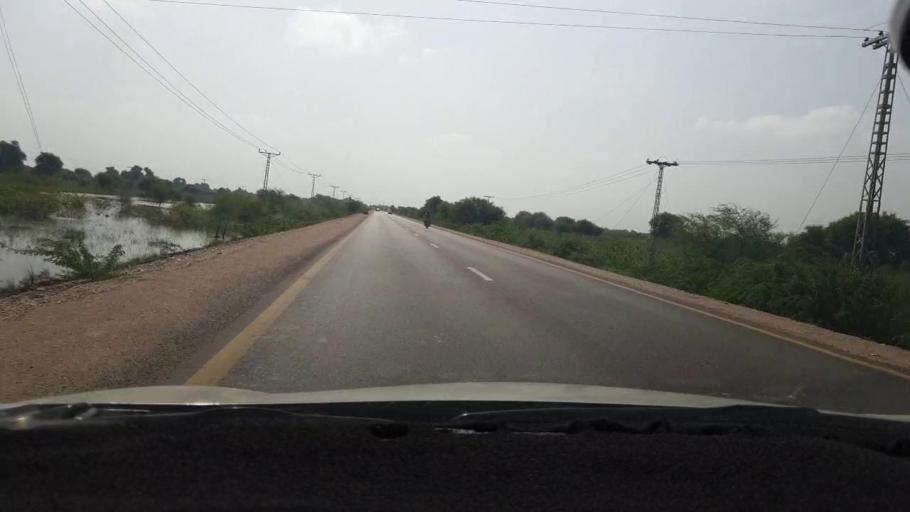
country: PK
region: Sindh
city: Mirpur Khas
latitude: 25.7338
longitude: 69.1026
